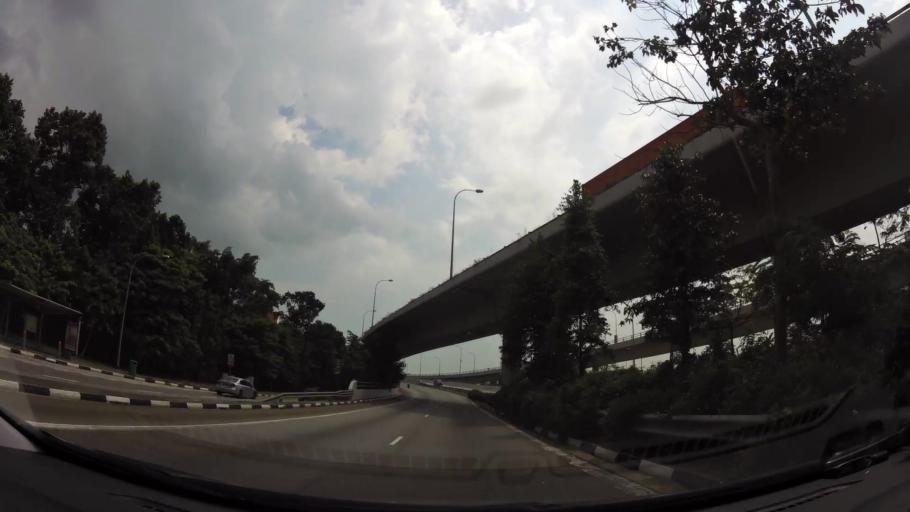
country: SG
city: Singapore
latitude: 1.2801
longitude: 103.7835
